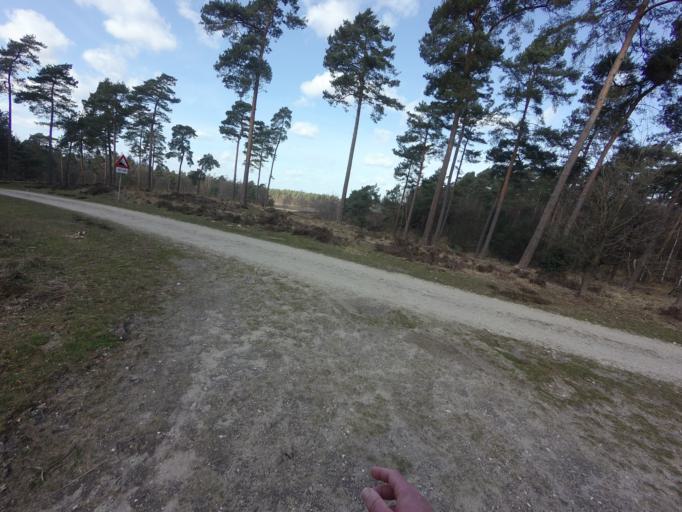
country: DE
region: North Rhine-Westphalia
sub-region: Regierungsbezirk Koln
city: Wassenberg
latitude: 51.1551
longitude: 6.1369
